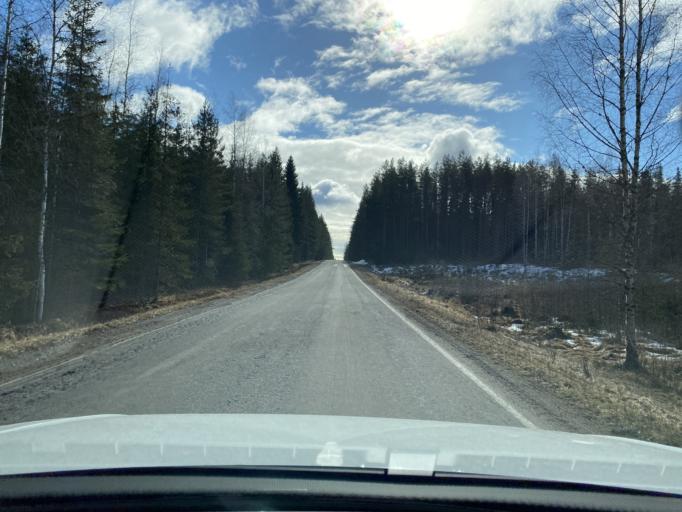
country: FI
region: Haeme
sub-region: Forssa
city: Tammela
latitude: 60.9669
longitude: 23.7152
